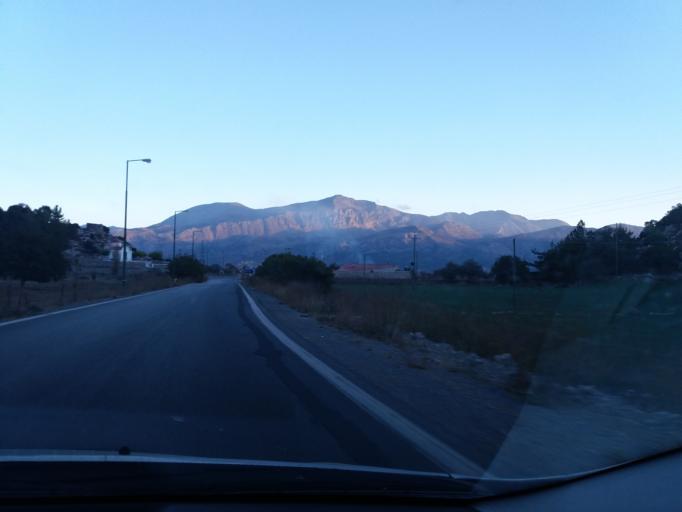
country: GR
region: Crete
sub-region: Nomos Irakleiou
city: Mokhos
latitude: 35.1985
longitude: 25.4615
